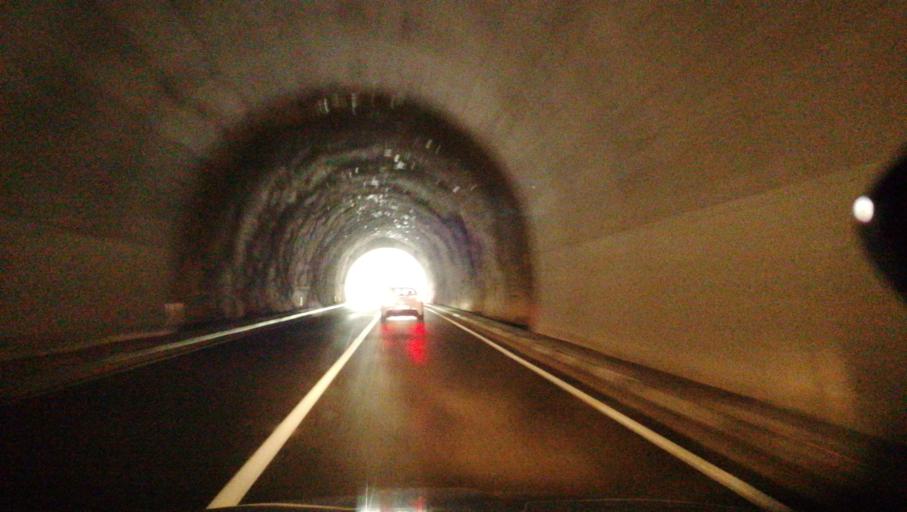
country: BA
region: Republika Srpska
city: Visegrad
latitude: 43.7465
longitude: 19.2200
